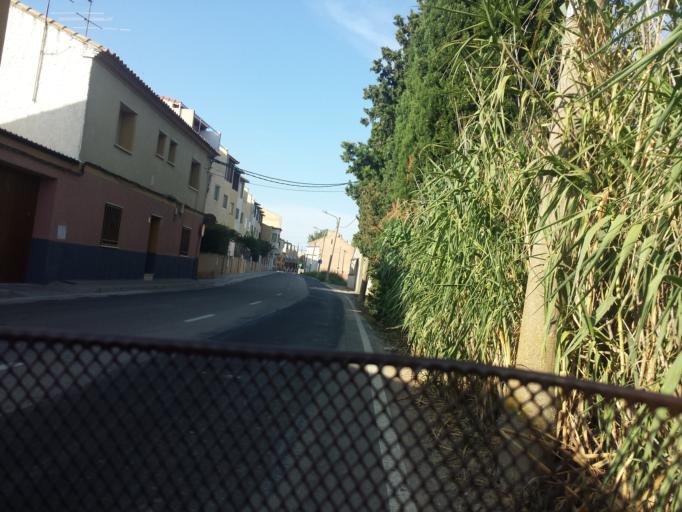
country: ES
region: Aragon
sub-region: Provincia de Zaragoza
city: Villanueva de Gallego
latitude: 41.7145
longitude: -0.8443
